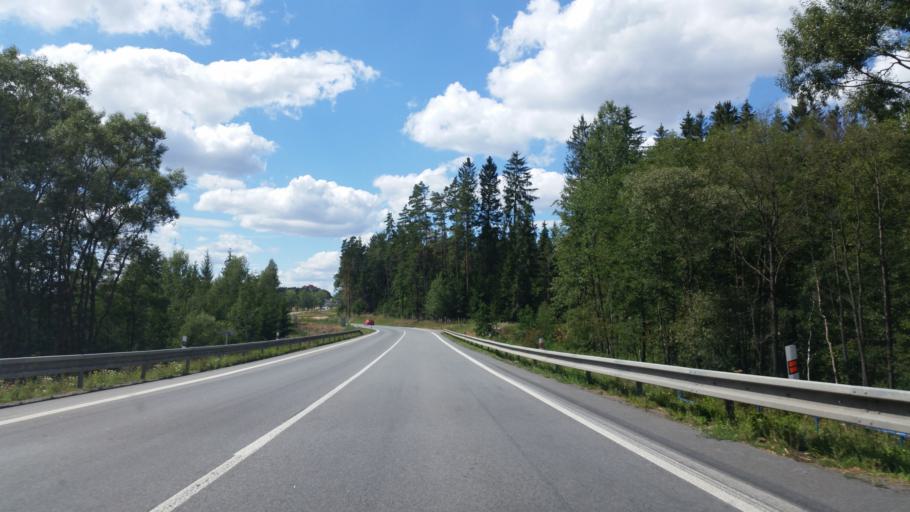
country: CZ
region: Vysocina
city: Pacov
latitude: 49.4254
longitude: 15.0342
